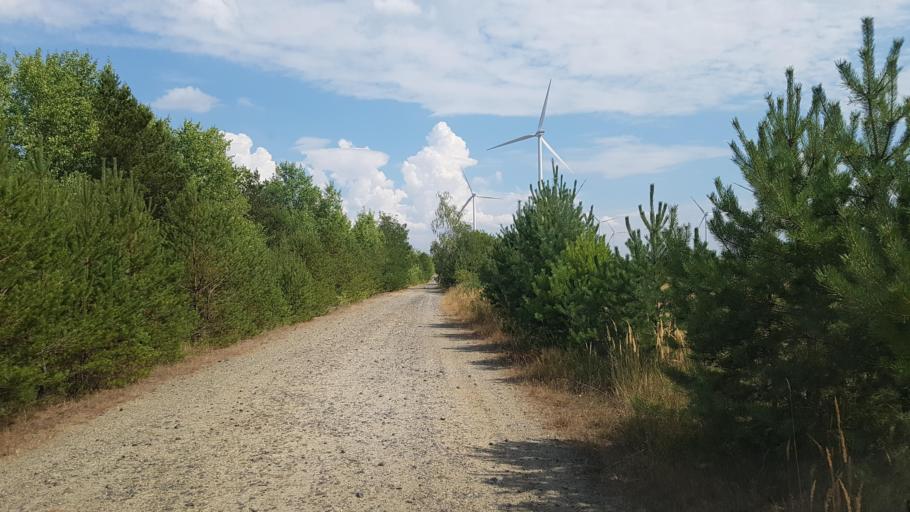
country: DE
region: Brandenburg
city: Sallgast
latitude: 51.5612
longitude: 13.8299
